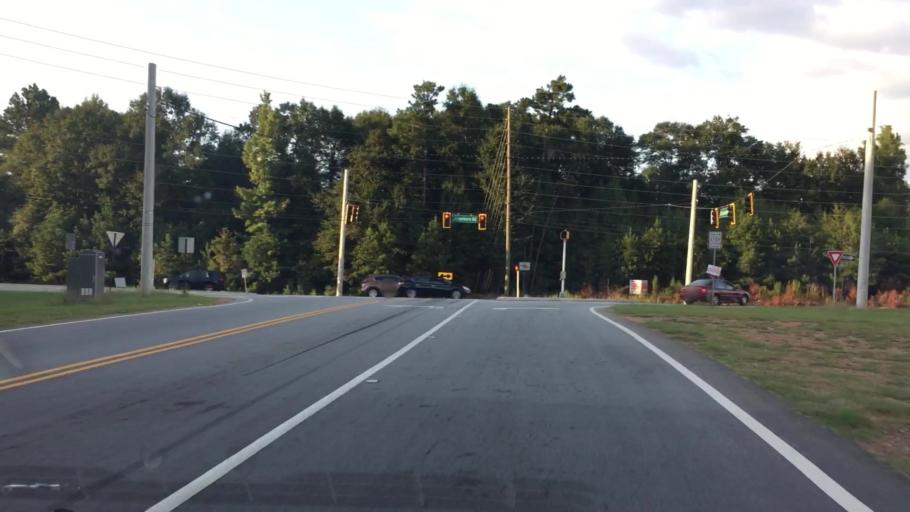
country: US
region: Georgia
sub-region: Henry County
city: McDonough
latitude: 33.4590
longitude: -84.1956
